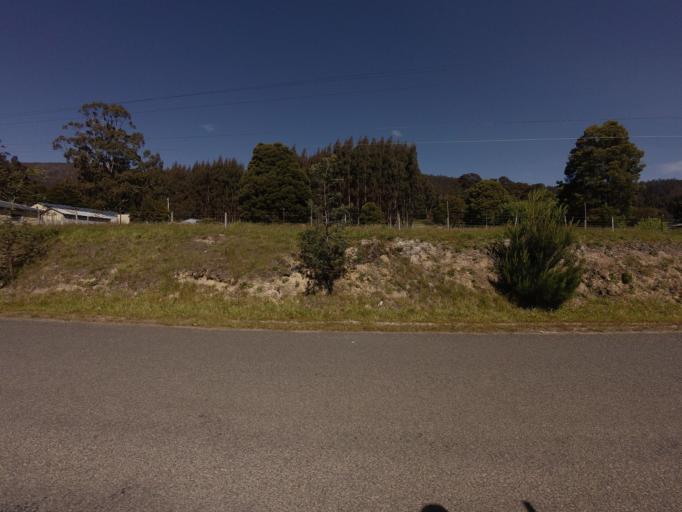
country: AU
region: Tasmania
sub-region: Derwent Valley
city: New Norfolk
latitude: -42.7529
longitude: 146.6342
